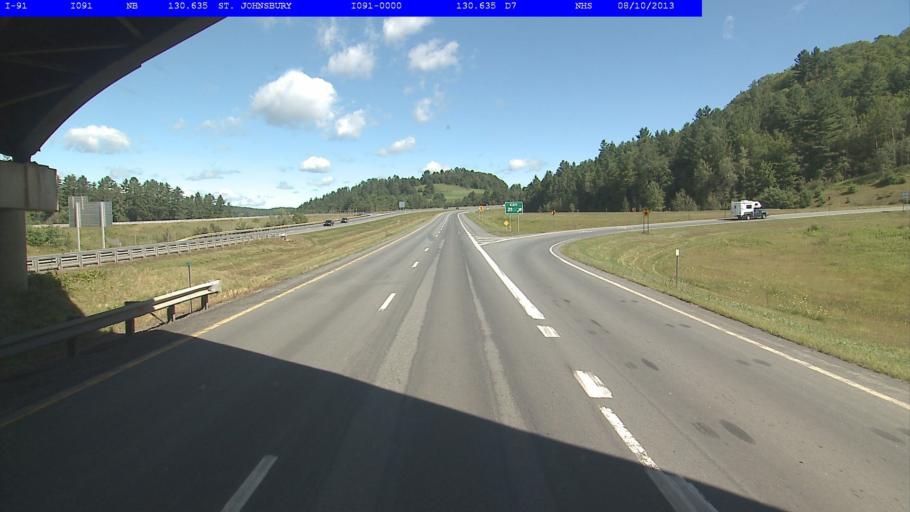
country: US
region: Vermont
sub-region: Caledonia County
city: St Johnsbury
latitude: 44.4283
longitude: -72.0336
